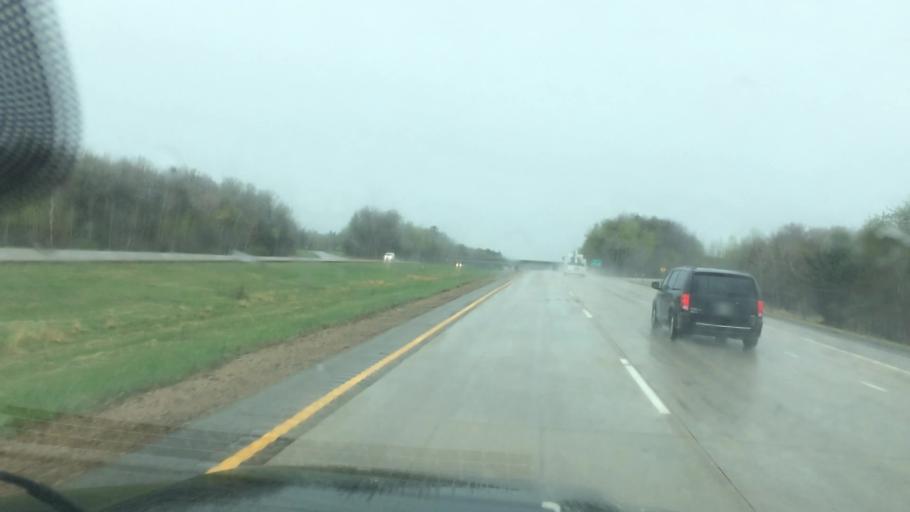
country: US
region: Wisconsin
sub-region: Marathon County
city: Mosinee
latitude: 44.6805
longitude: -89.6418
